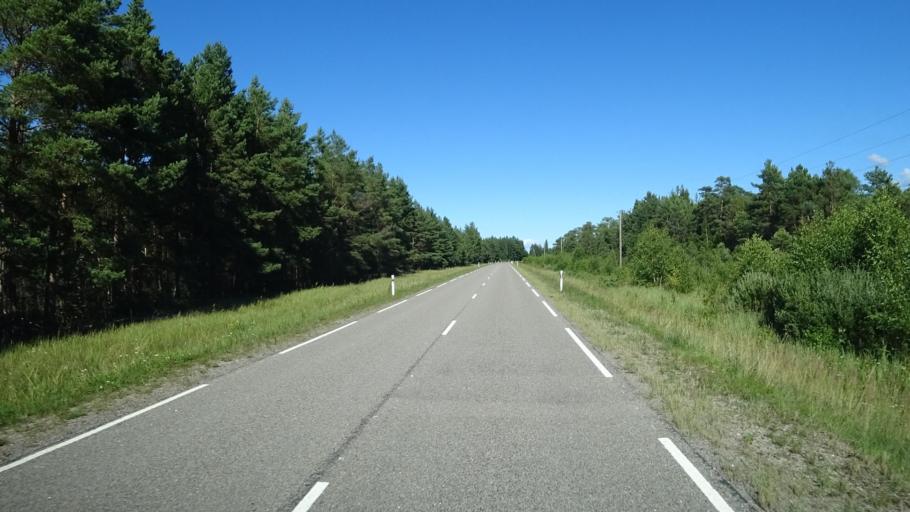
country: LV
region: Dundaga
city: Dundaga
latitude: 57.6969
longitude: 22.4044
